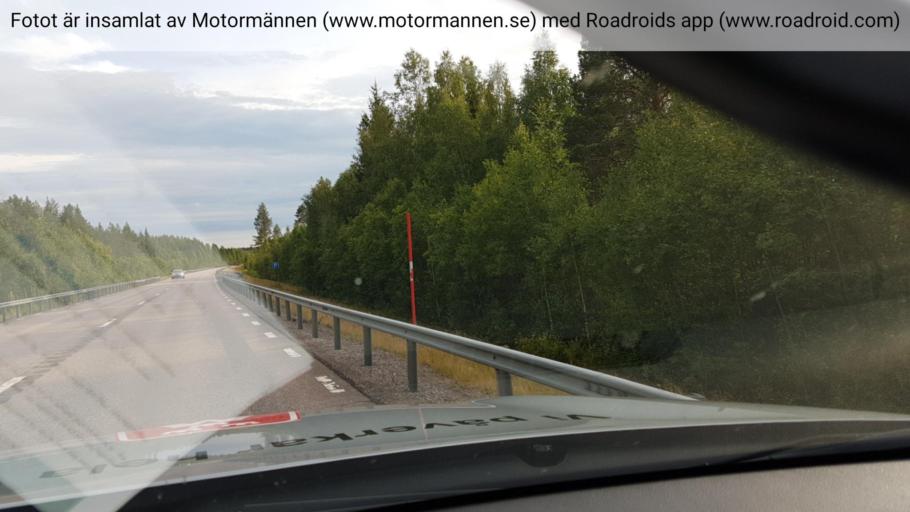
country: SE
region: Norrbotten
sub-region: Kalix Kommun
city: Toere
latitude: 65.9853
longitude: 22.6947
